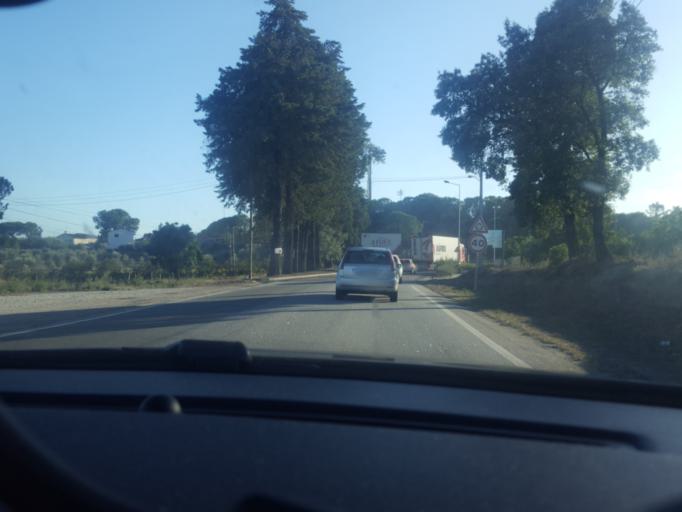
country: PT
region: Viseu
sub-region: Nelas
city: Nelas
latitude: 40.5434
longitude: -7.8440
